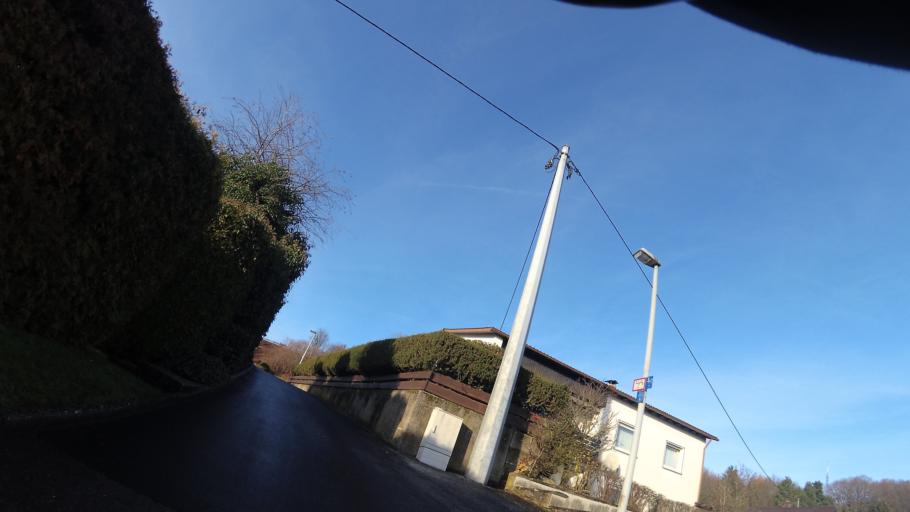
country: DE
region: Saarland
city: Spiesen-Elversberg
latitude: 49.3225
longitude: 7.1567
